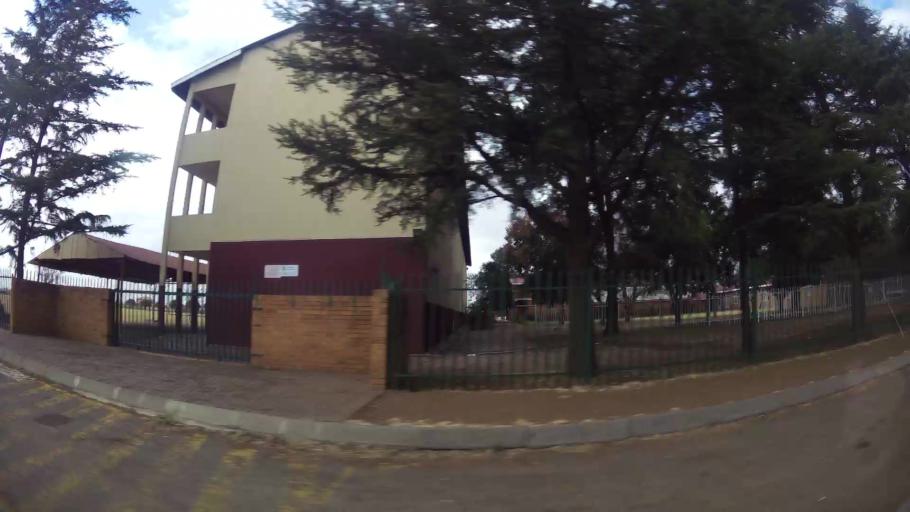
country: ZA
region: Gauteng
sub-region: Sedibeng District Municipality
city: Meyerton
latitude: -26.6012
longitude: 28.0464
